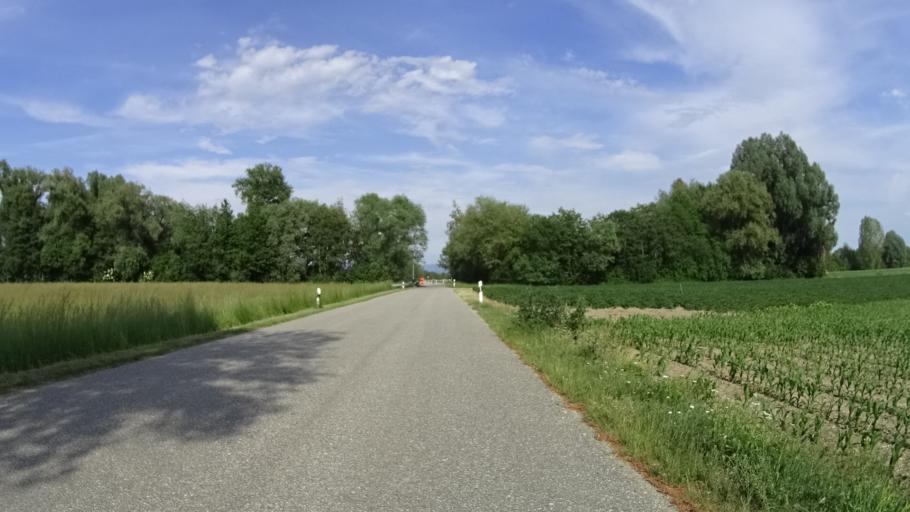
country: DE
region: Bavaria
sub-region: Lower Bavaria
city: Kirchroth
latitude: 48.9406
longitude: 12.5307
